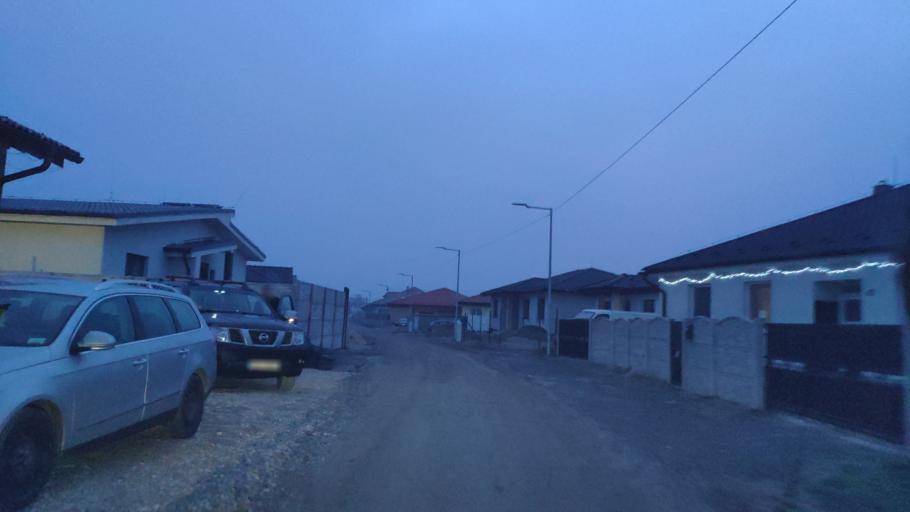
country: SK
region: Kosicky
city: Kosice
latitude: 48.6148
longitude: 21.3317
